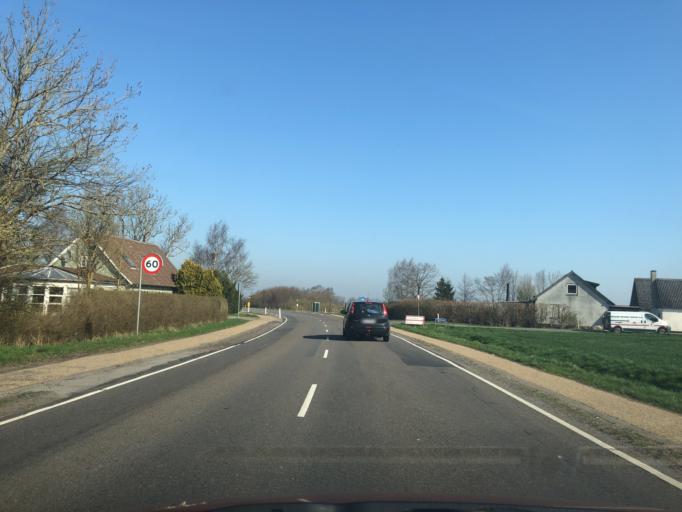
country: DK
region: Zealand
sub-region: Ringsted Kommune
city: Ringsted
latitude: 55.3941
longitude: 11.8402
